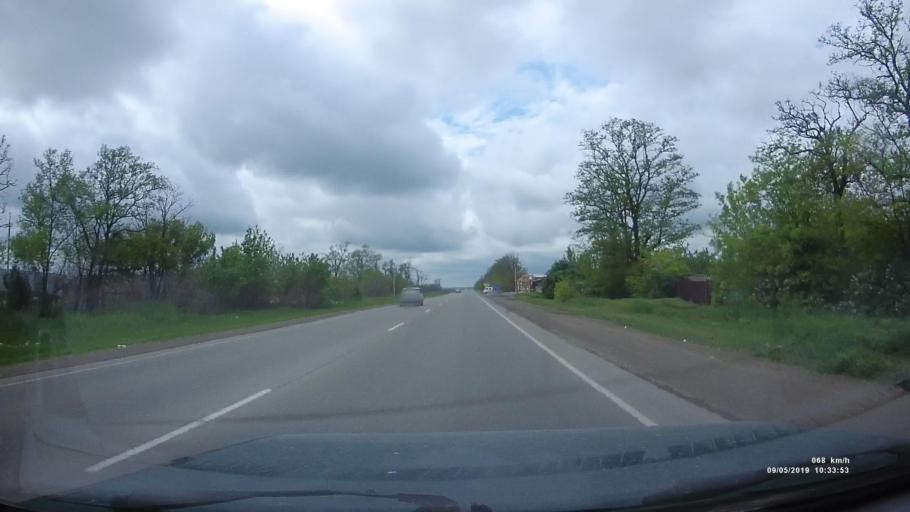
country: RU
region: Rostov
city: Azov
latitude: 47.0599
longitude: 39.4233
